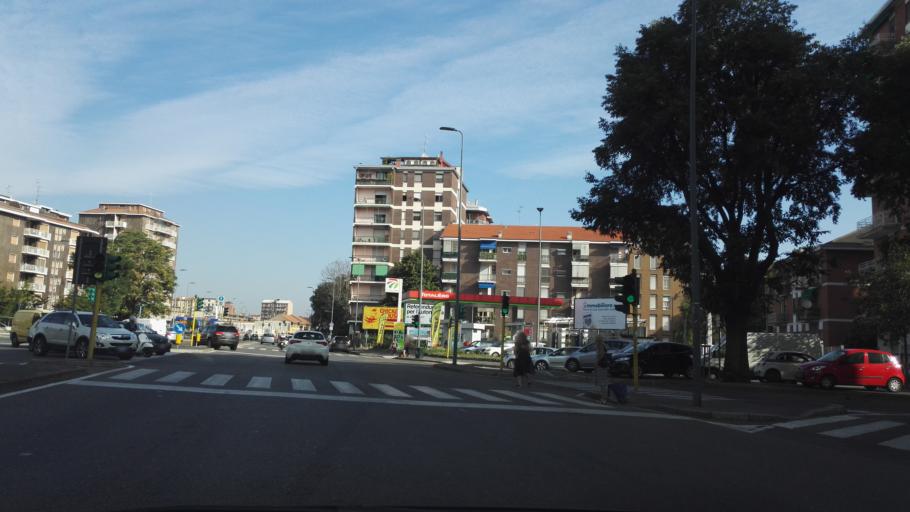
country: IT
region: Lombardy
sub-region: Citta metropolitana di Milano
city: Romano Banco
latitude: 45.4407
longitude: 9.1506
